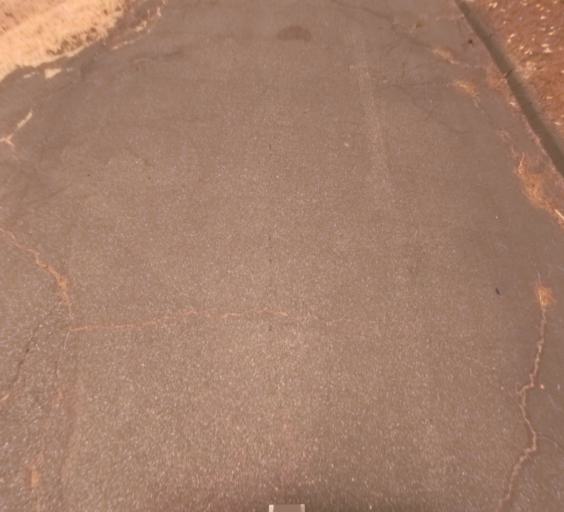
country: US
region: California
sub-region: Madera County
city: Oakhurst
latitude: 37.3661
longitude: -119.6186
